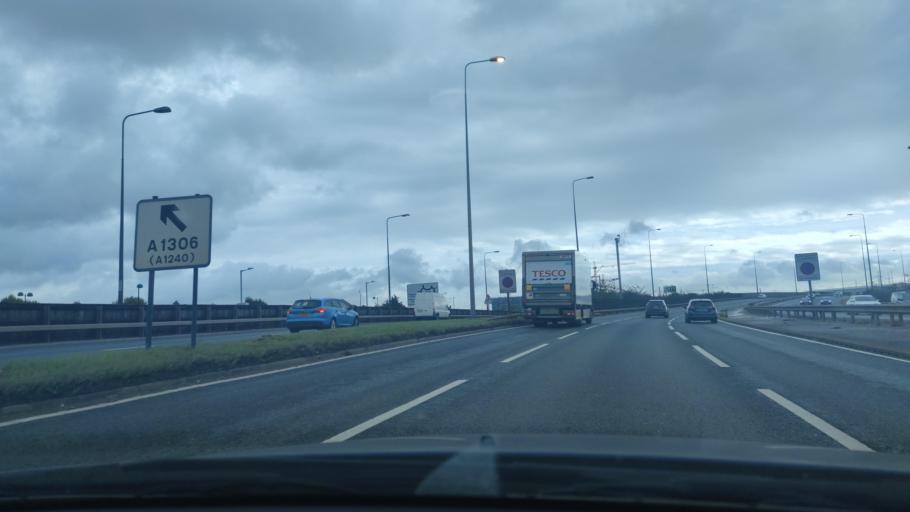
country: GB
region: England
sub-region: Greater London
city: Becontree
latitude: 51.5316
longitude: 0.1361
